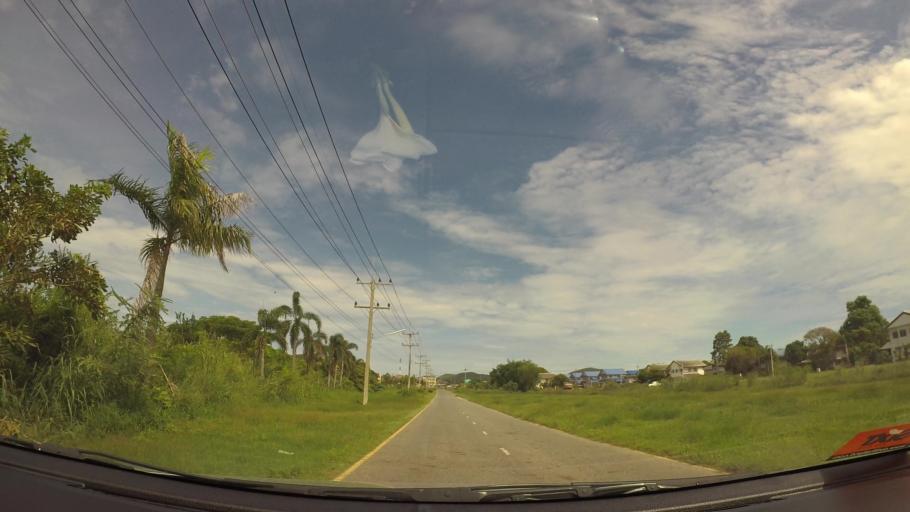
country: TH
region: Chon Buri
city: Sattahip
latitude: 12.6684
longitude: 100.9069
